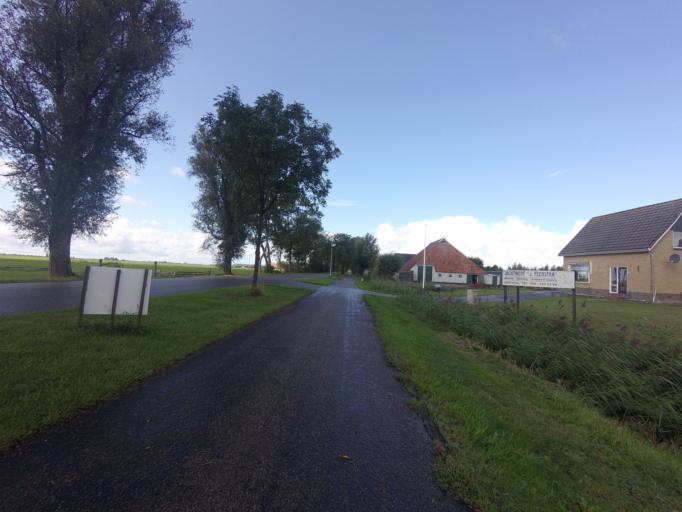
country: NL
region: Friesland
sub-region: Gemeente Boarnsterhim
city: Warten
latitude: 53.1496
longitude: 5.8840
